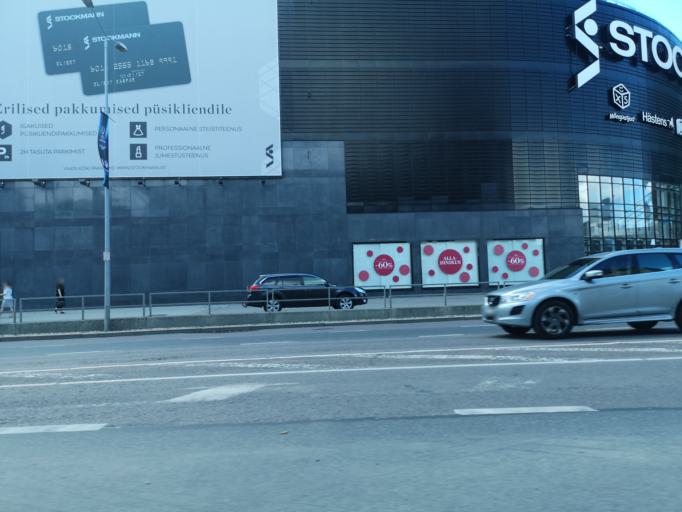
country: EE
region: Harju
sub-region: Tallinna linn
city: Tallinn
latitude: 59.4323
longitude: 24.7625
